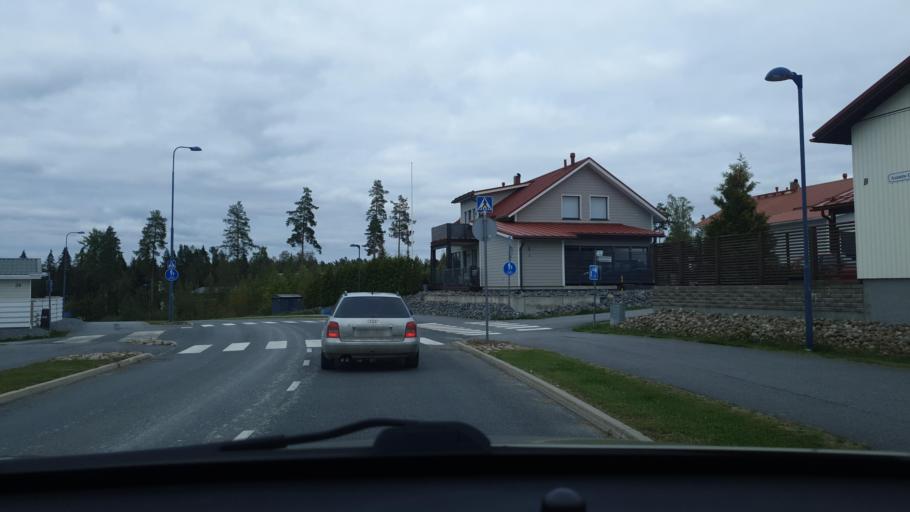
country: FI
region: Ostrobothnia
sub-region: Vaasa
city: Korsholm
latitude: 63.1252
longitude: 21.6633
